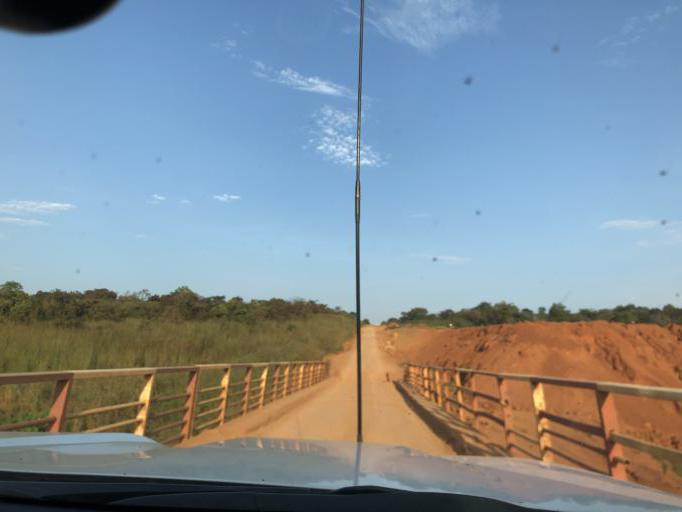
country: CF
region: Nana-Mambere
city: Bouar
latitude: 5.8947
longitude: 15.7598
